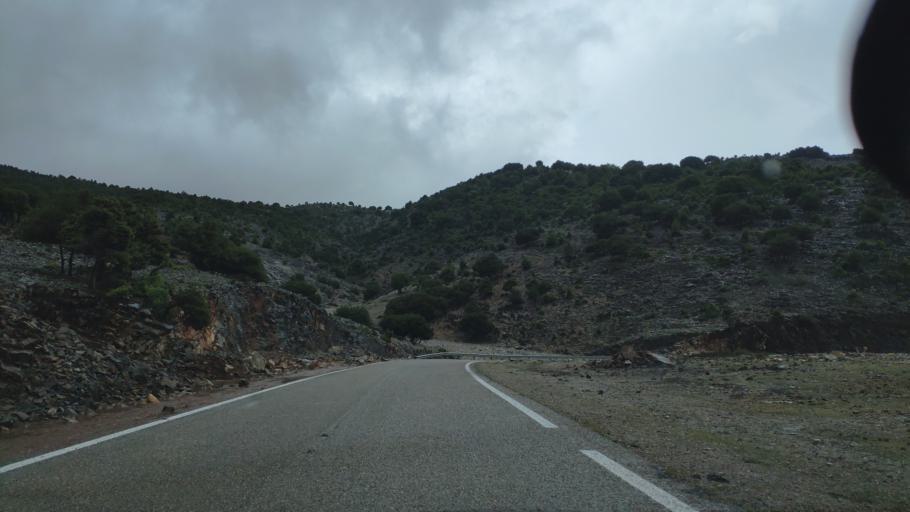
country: GR
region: West Greece
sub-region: Nomos Aitolias kai Akarnanias
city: Krikellos
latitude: 39.0793
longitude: 21.3978
